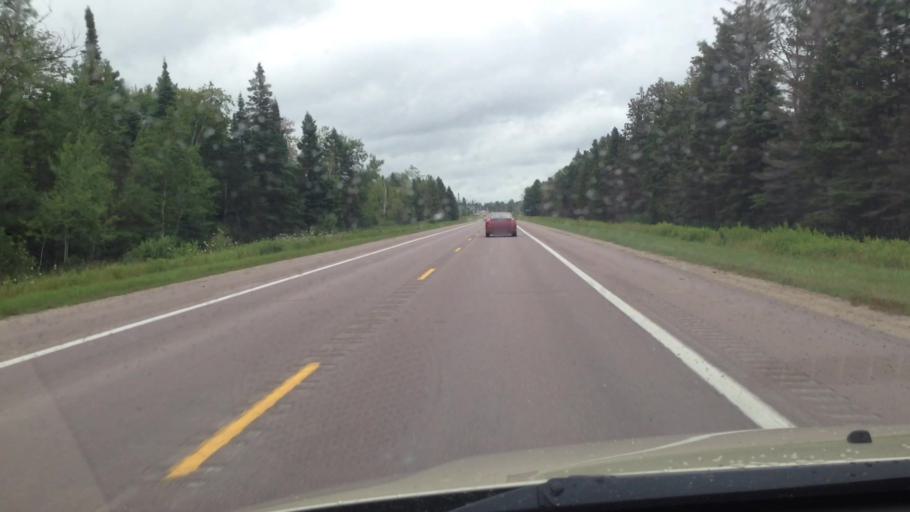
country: US
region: Michigan
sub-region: Schoolcraft County
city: Manistique
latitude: 45.9909
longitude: -86.0273
